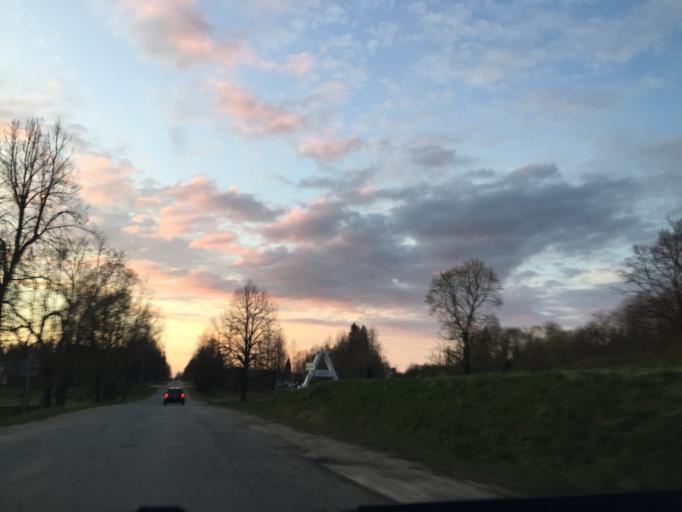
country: LV
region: Aluksnes Rajons
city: Aluksne
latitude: 57.4028
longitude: 27.0466
